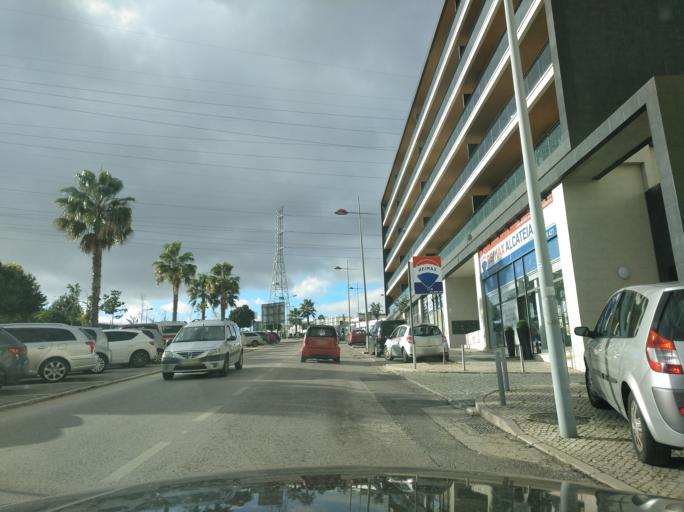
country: PT
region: Lisbon
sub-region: Loures
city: Sacavem
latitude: 38.7951
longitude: -9.1146
